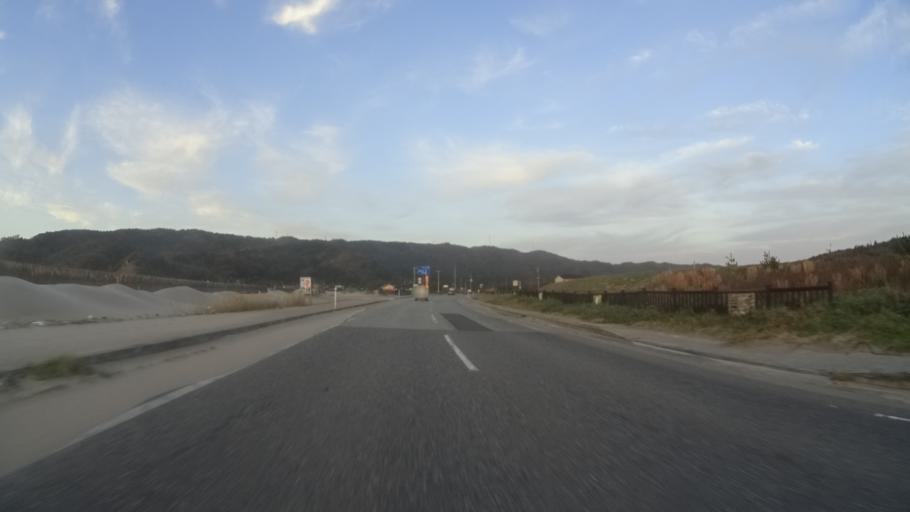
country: JP
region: Ishikawa
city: Nanao
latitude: 37.2862
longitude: 136.7358
